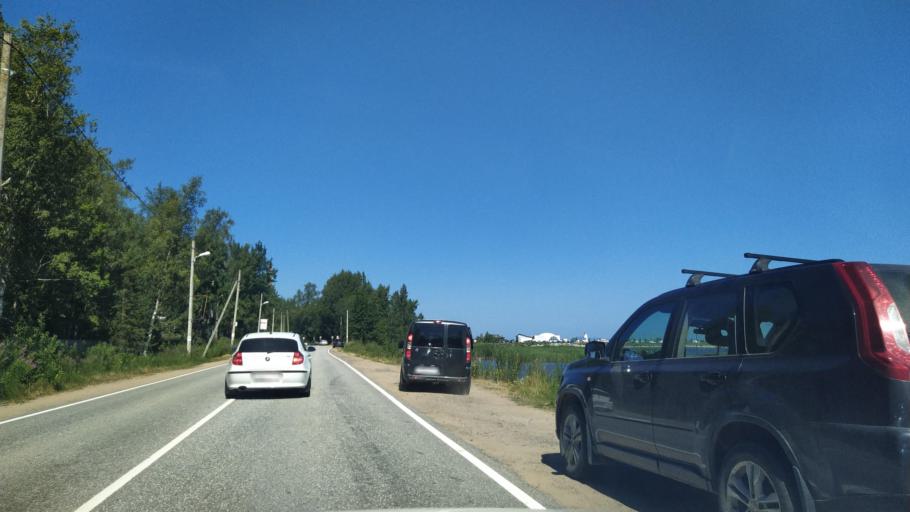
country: RU
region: Leningrad
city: Borisova Griva
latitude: 60.1132
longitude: 31.0841
